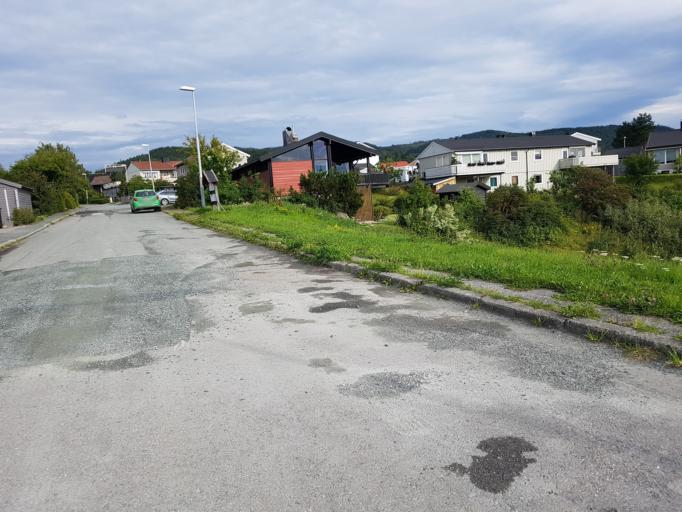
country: NO
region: Sor-Trondelag
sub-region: Trondheim
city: Trondheim
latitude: 63.3879
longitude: 10.4238
